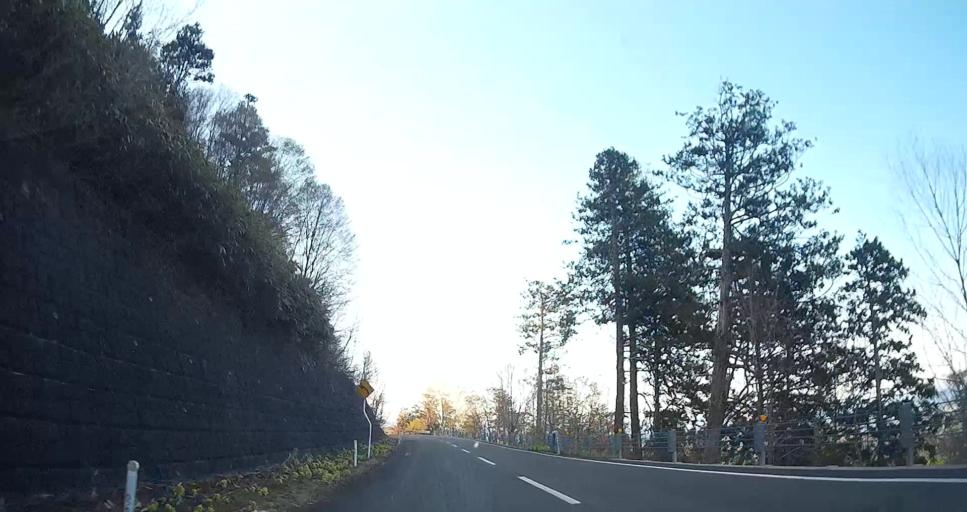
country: JP
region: Aomori
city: Mutsu
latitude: 41.3108
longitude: 141.1129
